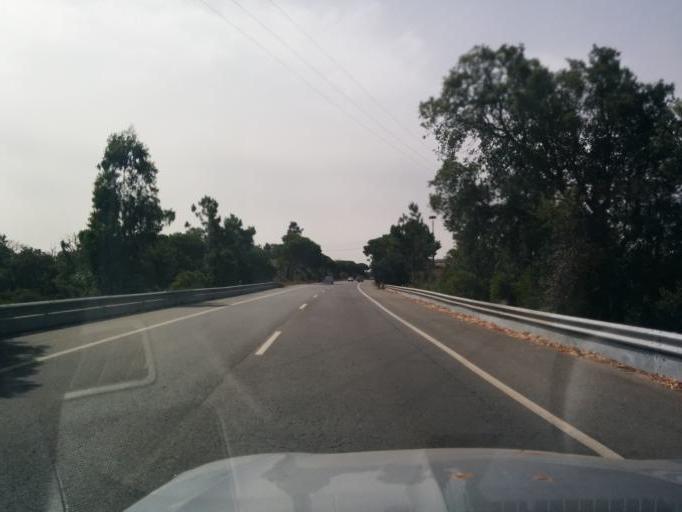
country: PT
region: Beja
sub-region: Odemira
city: Vila Nova de Milfontes
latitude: 37.7216
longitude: -8.7674
